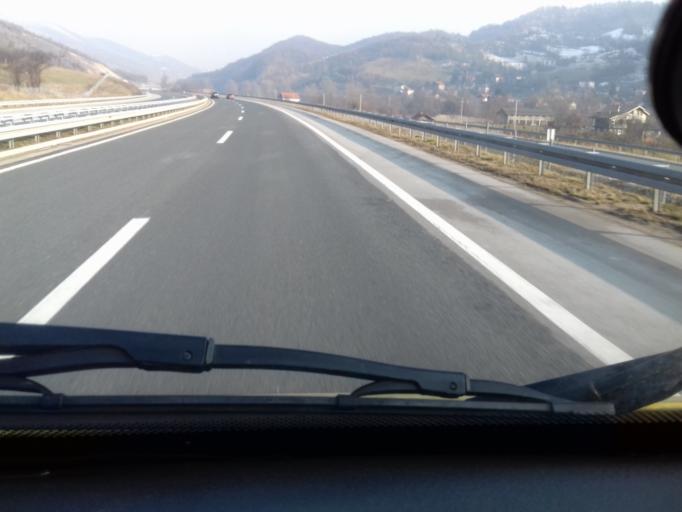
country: BA
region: Federation of Bosnia and Herzegovina
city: Kacuni
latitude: 44.1334
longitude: 18.0139
